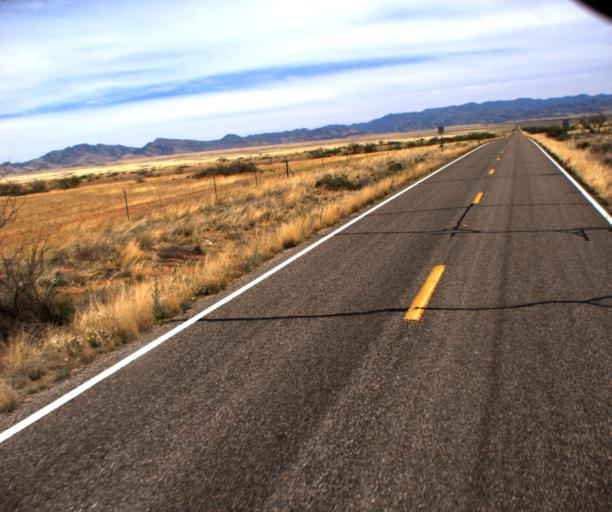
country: US
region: Arizona
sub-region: Cochise County
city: Willcox
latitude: 32.0913
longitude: -109.5321
